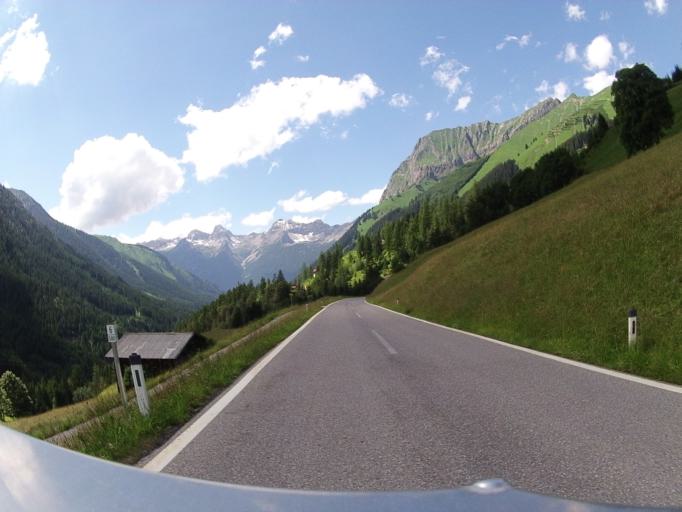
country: AT
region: Tyrol
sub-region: Politischer Bezirk Reutte
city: Elmen
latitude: 47.3053
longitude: 10.5915
